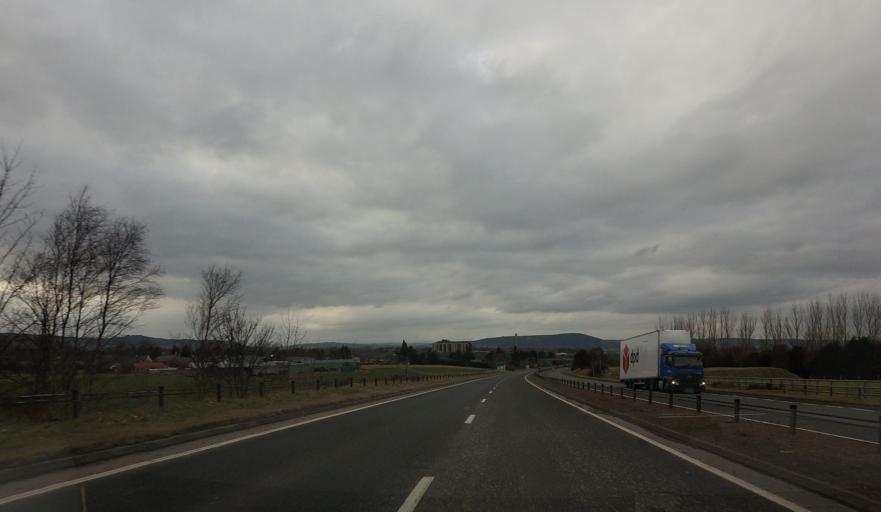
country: GB
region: Scotland
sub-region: Highland
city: Inverness
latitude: 57.4681
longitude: -4.1799
